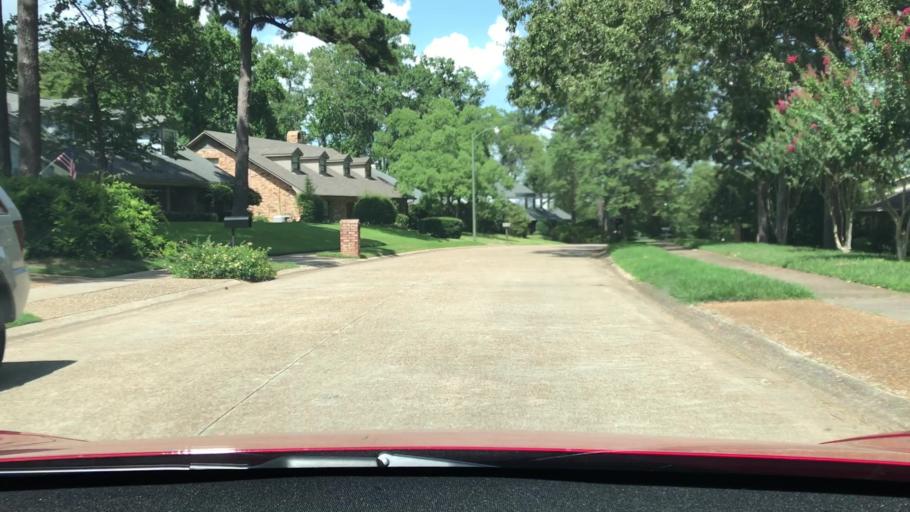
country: US
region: Louisiana
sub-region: Bossier Parish
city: Bossier City
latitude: 32.4295
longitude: -93.7299
